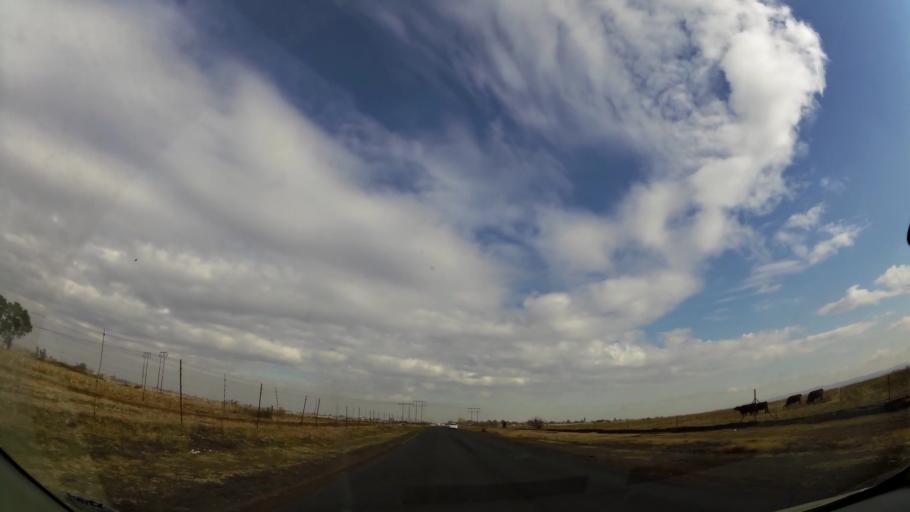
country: ZA
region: Gauteng
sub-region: Sedibeng District Municipality
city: Meyerton
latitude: -26.5581
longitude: 28.0525
